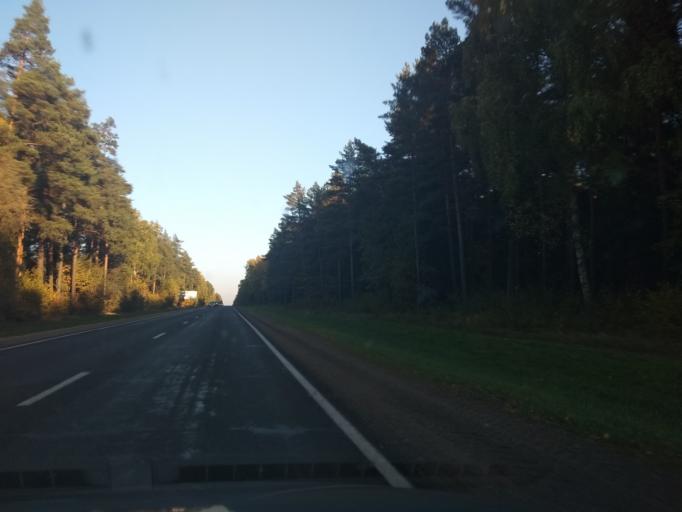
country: BY
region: Grodnenskaya
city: Vawkavysk
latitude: 53.1466
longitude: 24.5194
